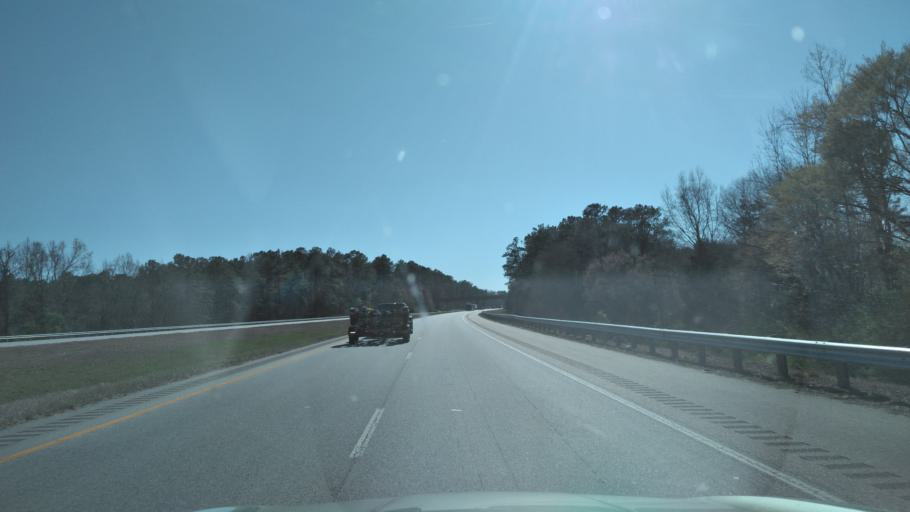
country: US
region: Alabama
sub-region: Lowndes County
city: Fort Deposit
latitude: 31.9636
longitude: -86.5398
